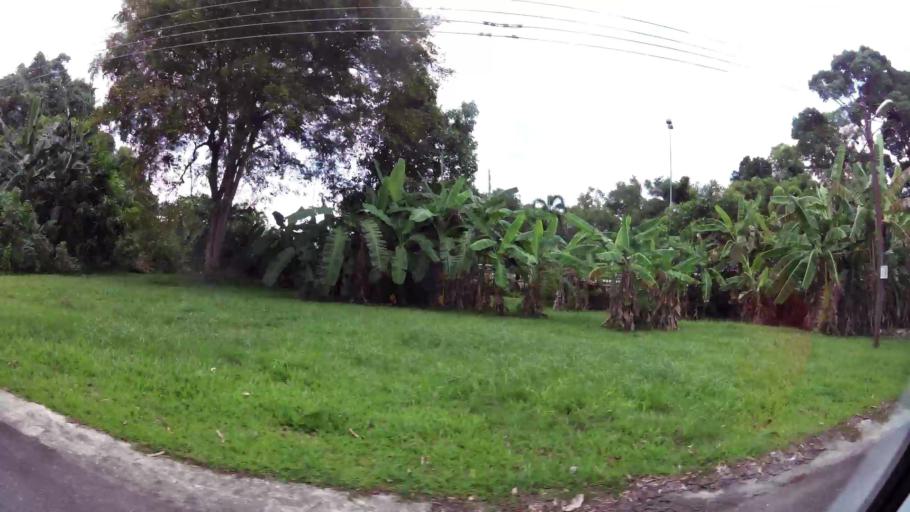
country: BN
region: Brunei and Muara
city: Bandar Seri Begawan
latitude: 4.9523
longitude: 114.9597
